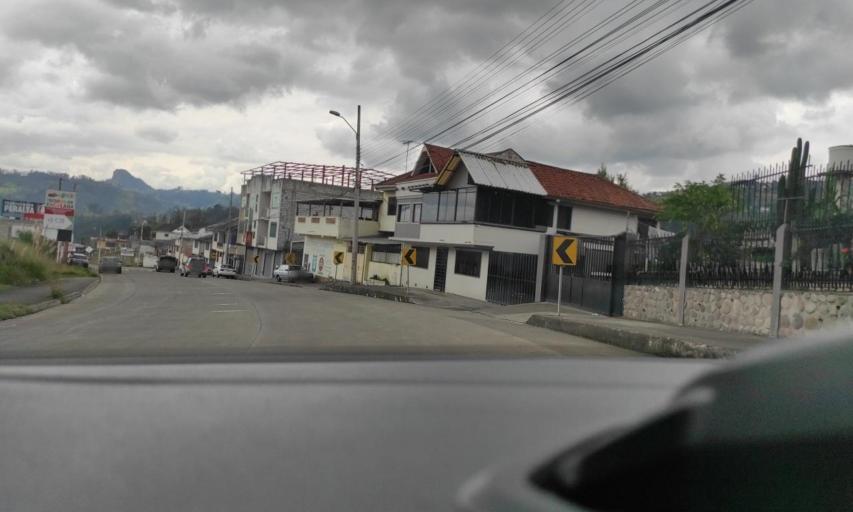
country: EC
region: Canar
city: Azogues
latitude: -2.7040
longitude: -78.8926
